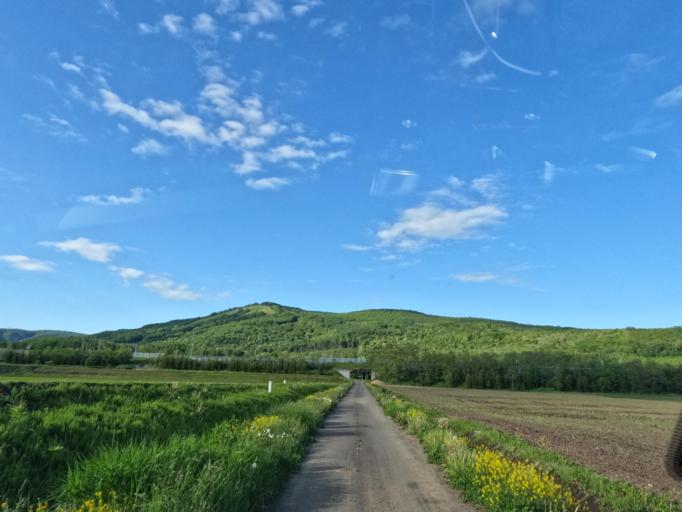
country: JP
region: Hokkaido
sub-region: Asahikawa-shi
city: Asahikawa
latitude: 43.9194
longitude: 142.4934
